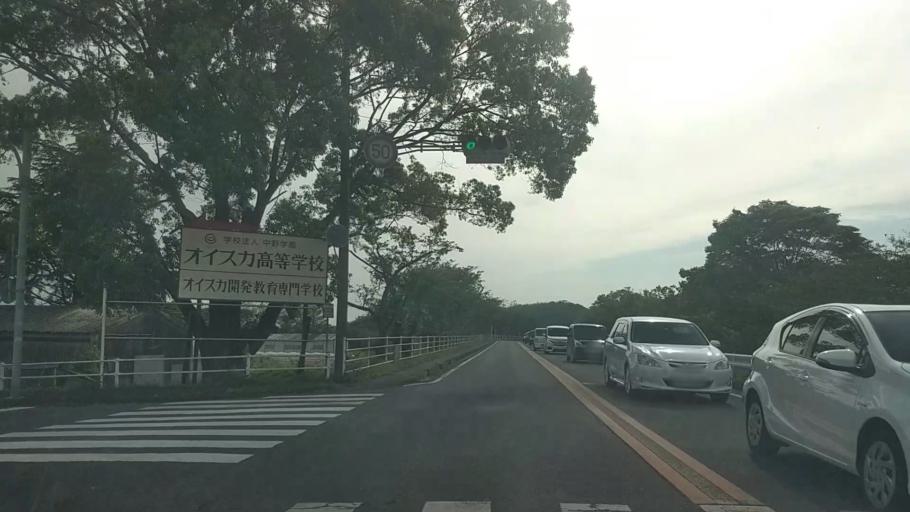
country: JP
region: Shizuoka
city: Hamamatsu
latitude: 34.7613
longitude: 137.6537
